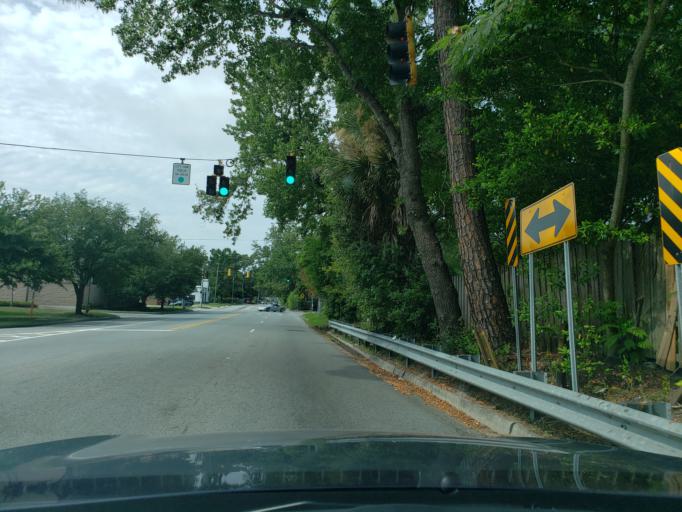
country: US
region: Georgia
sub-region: Chatham County
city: Thunderbolt
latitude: 32.0365
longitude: -81.0902
